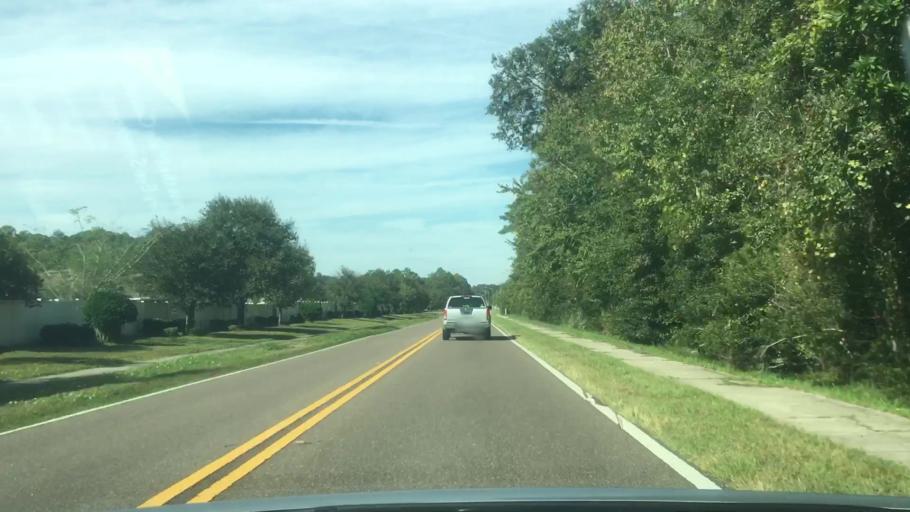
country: US
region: Florida
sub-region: Nassau County
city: Yulee
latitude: 30.4864
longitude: -81.6152
